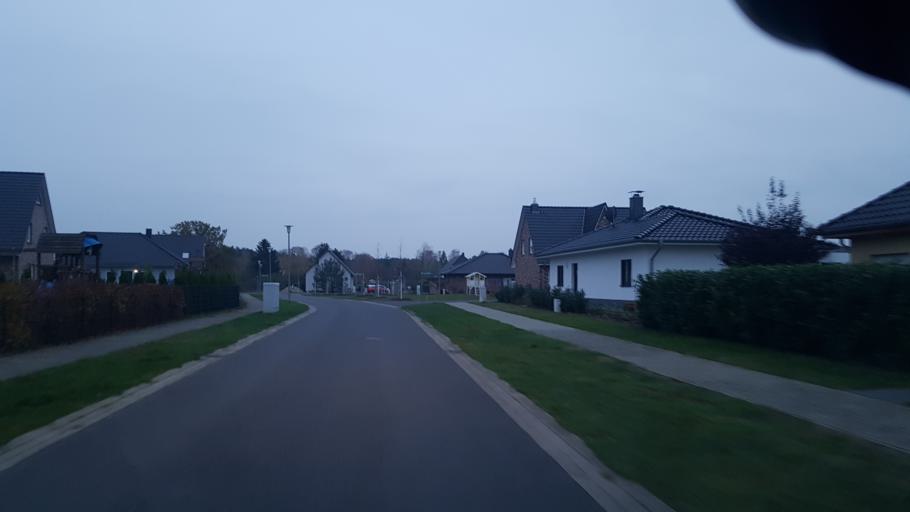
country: DE
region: Brandenburg
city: Nauen
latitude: 52.6863
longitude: 12.9407
